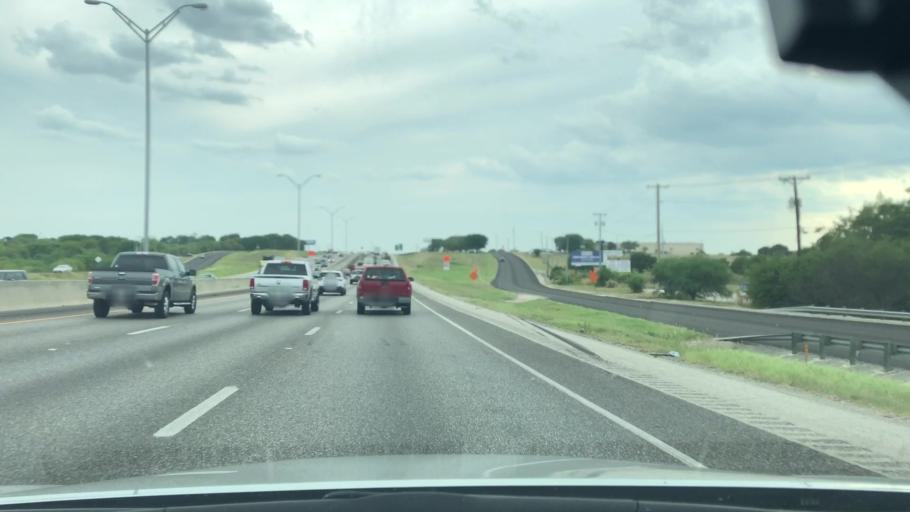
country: US
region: Texas
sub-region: Guadalupe County
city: Northcliff
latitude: 29.6361
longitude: -98.2199
